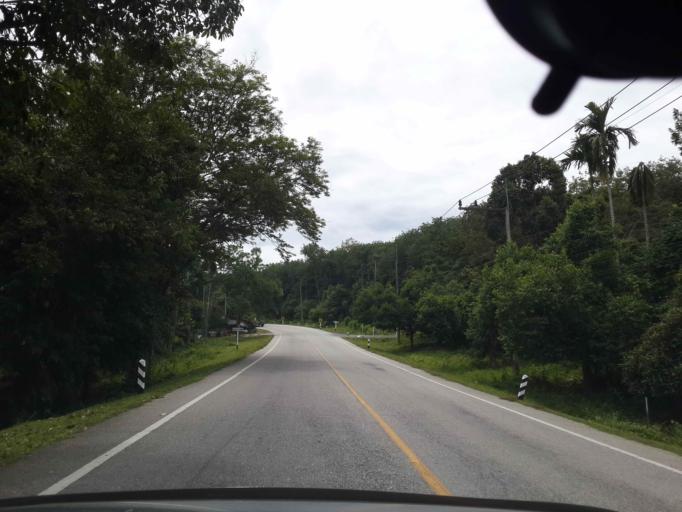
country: TH
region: Narathiwat
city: Rueso
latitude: 6.3650
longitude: 101.6020
